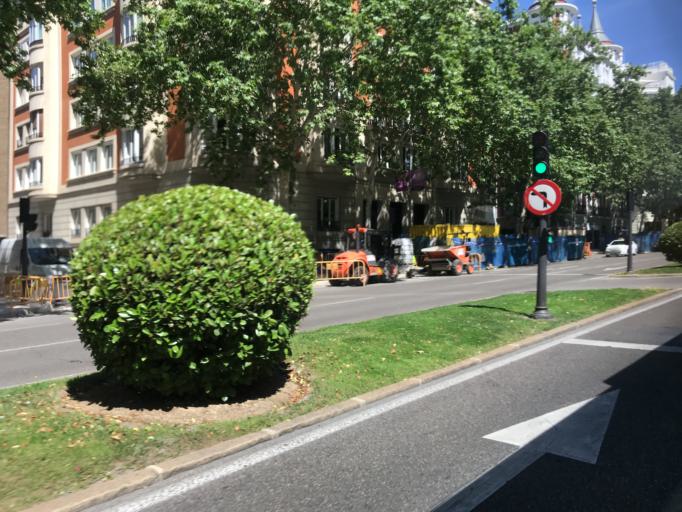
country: ES
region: Madrid
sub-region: Provincia de Madrid
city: Retiro
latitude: 40.4137
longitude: -3.6888
